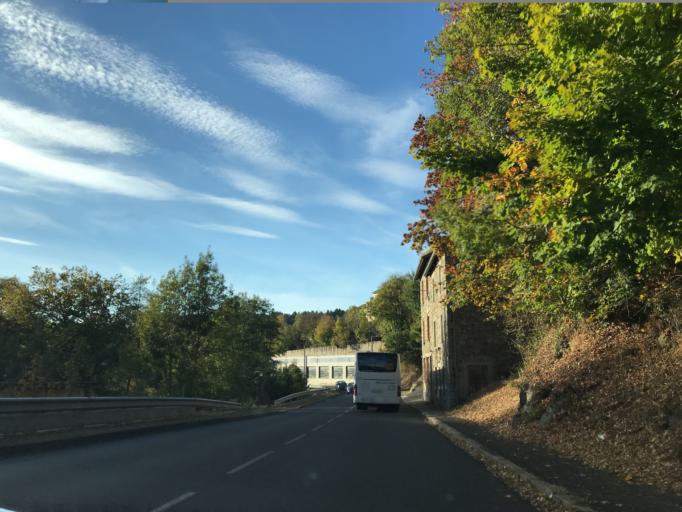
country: FR
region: Auvergne
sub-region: Departement du Puy-de-Dome
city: La Monnerie-le-Montel
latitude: 45.8685
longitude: 3.6026
